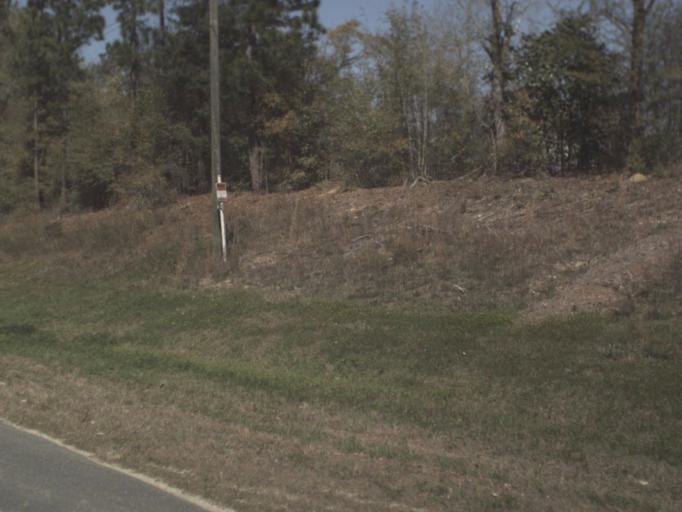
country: US
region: Florida
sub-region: Jackson County
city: Graceville
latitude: 30.9673
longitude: -85.6055
